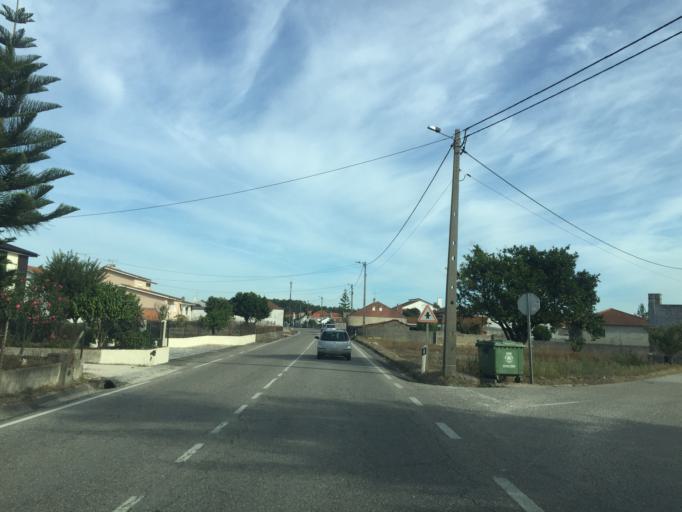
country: PT
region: Leiria
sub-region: Pombal
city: Lourical
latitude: 39.9808
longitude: -8.7987
